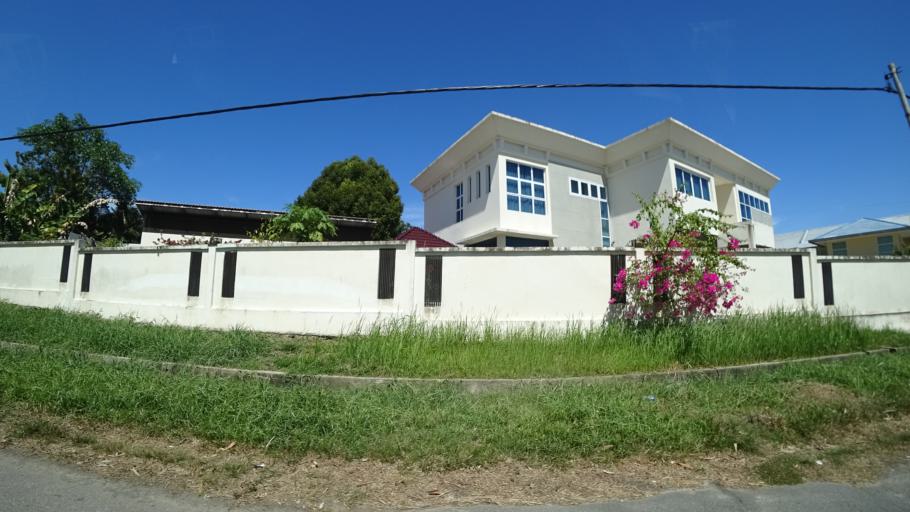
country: BN
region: Brunei and Muara
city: Bandar Seri Begawan
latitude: 4.9183
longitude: 114.9160
